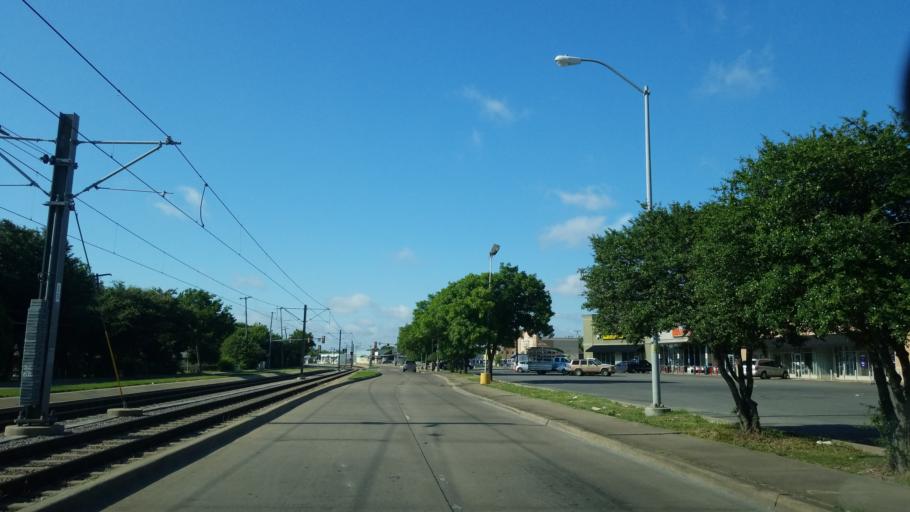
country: US
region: Texas
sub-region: Dallas County
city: Dallas
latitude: 32.7148
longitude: -96.8045
